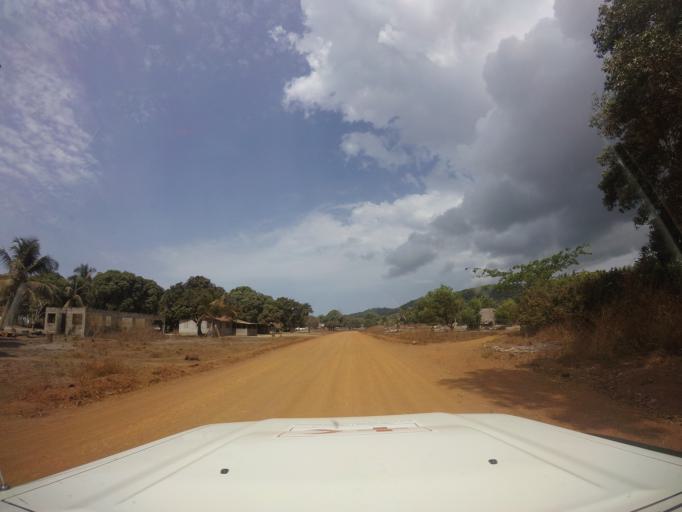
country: LR
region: Grand Cape Mount
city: Robertsport
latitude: 6.7056
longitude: -11.3314
